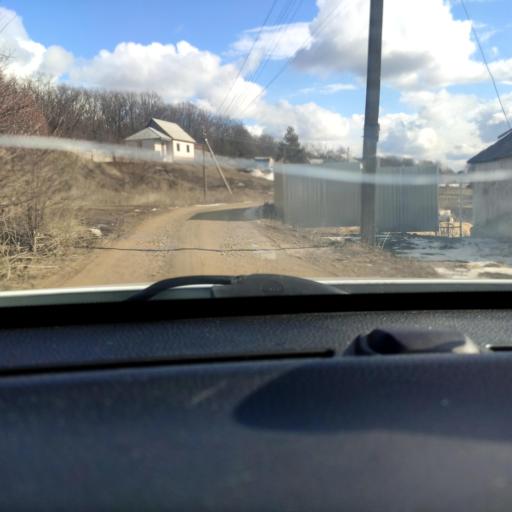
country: RU
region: Voronezj
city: Somovo
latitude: 51.6905
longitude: 39.3823
